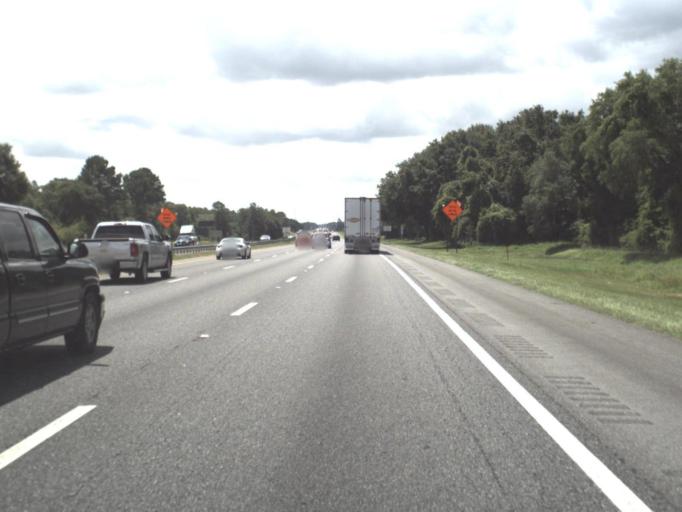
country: US
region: Florida
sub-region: Columbia County
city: Lake City
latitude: 30.1352
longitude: -82.6660
